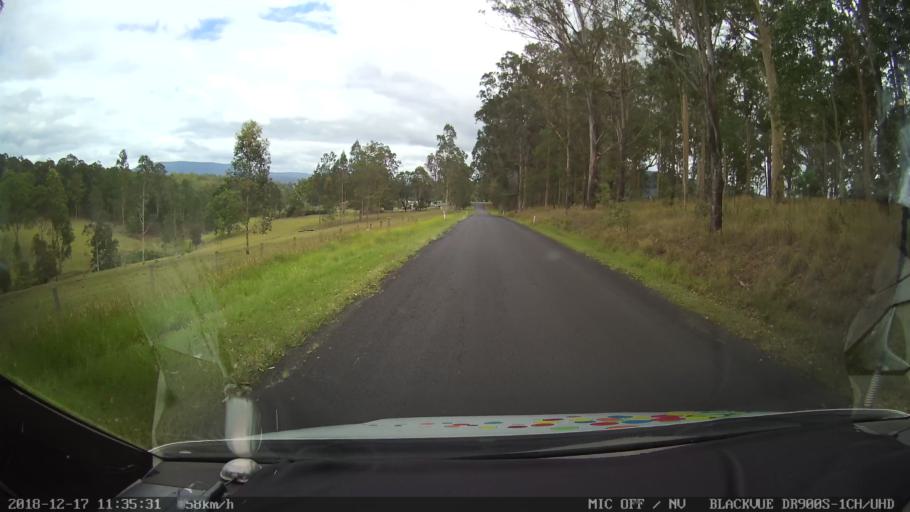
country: AU
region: New South Wales
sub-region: Kyogle
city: Kyogle
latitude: -28.7221
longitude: 152.6065
